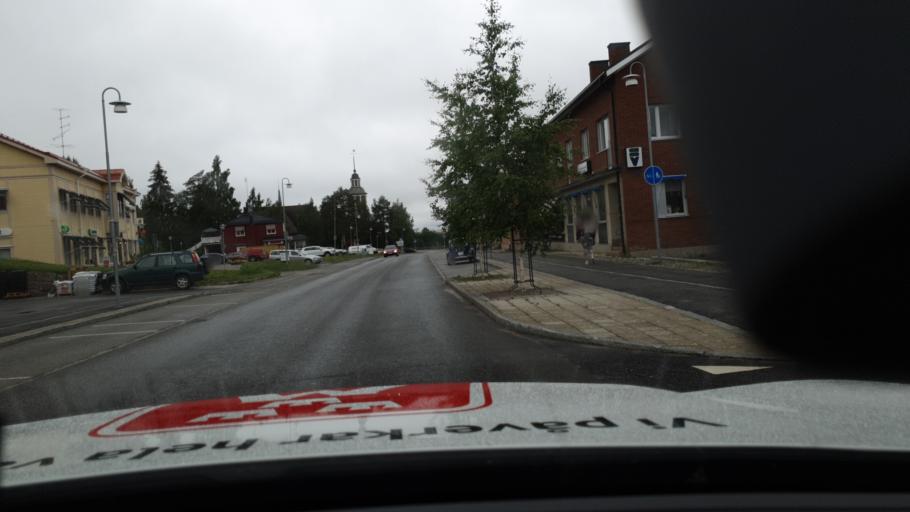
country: SE
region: Norrbotten
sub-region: Overtornea Kommun
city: OEvertornea
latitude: 66.3886
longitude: 23.6578
